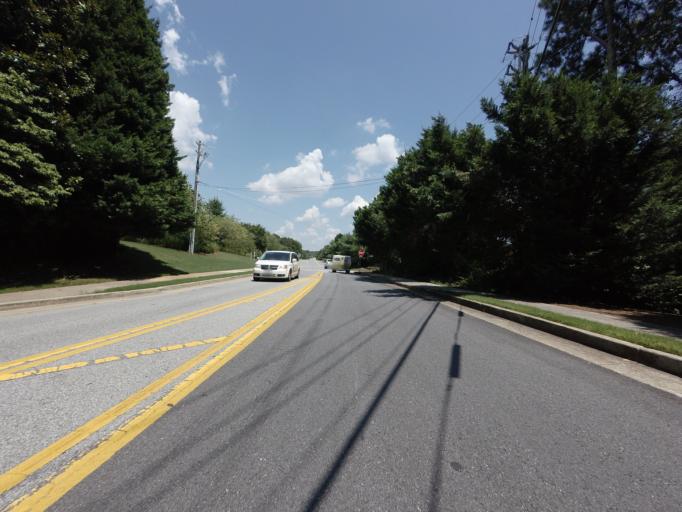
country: US
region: Georgia
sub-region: Fulton County
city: Johns Creek
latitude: 34.0408
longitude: -84.2240
